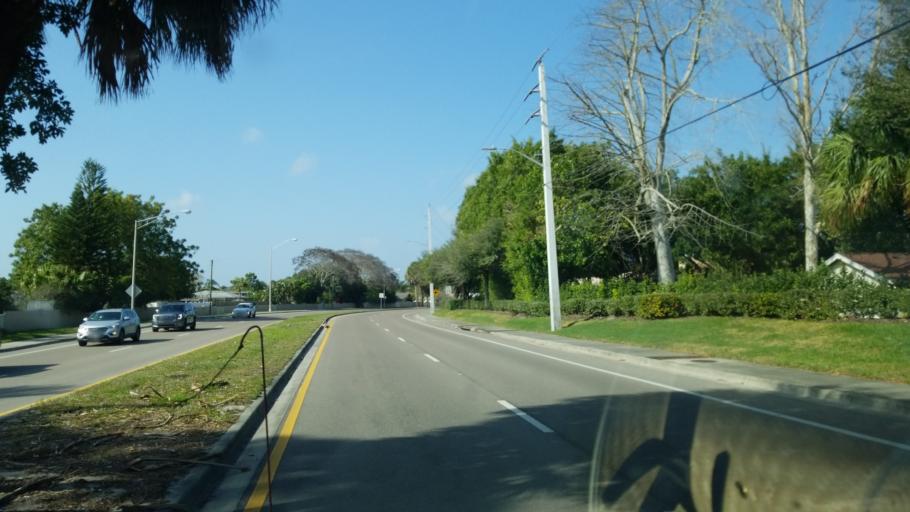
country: US
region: Florida
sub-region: Sarasota County
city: Sarasota Springs
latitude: 27.3164
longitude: -82.4824
